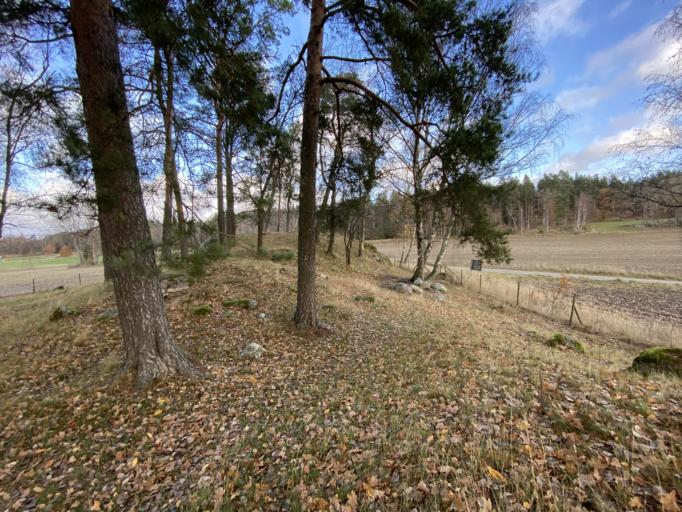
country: SE
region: Stockholm
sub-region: Botkyrka Kommun
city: Eriksberg
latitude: 59.2249
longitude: 17.8270
